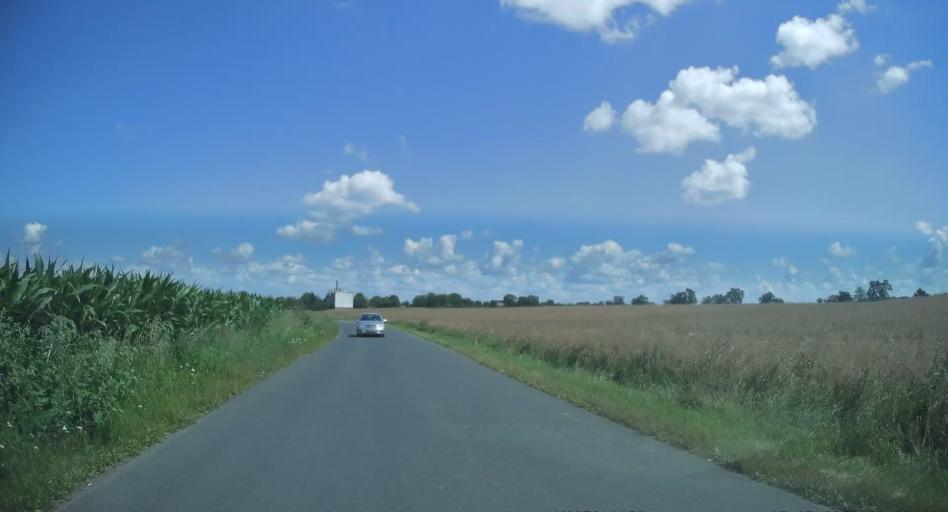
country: PL
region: Subcarpathian Voivodeship
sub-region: Powiat jaroslawski
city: Sosnica
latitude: 49.8567
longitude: 22.8799
